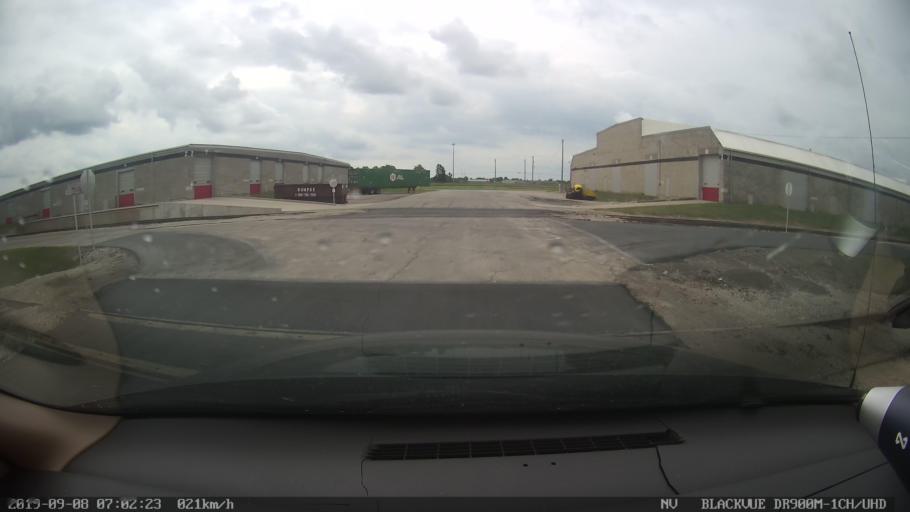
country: US
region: Ohio
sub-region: Richland County
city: Shelby
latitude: 40.8994
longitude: -82.6719
